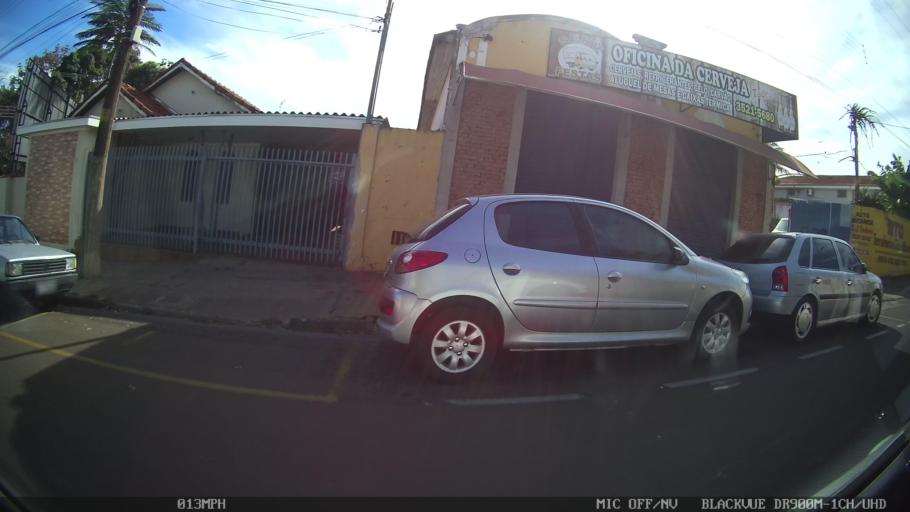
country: BR
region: Sao Paulo
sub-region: Catanduva
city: Catanduva
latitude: -21.1292
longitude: -48.9767
